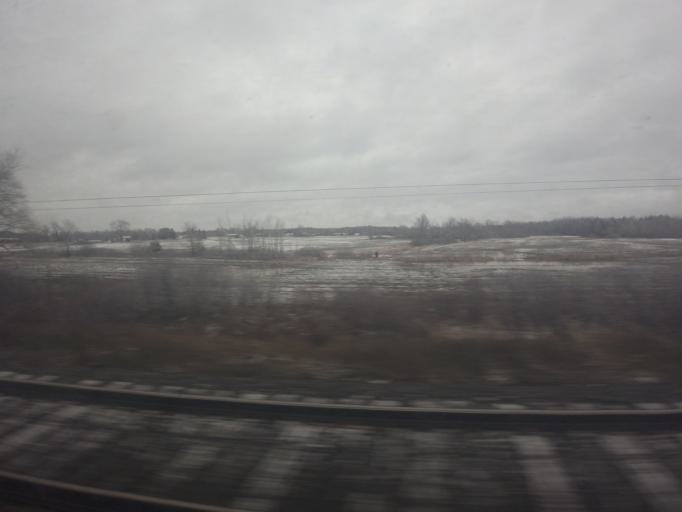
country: US
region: New York
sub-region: Jefferson County
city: Alexandria Bay
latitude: 44.3998
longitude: -76.0240
